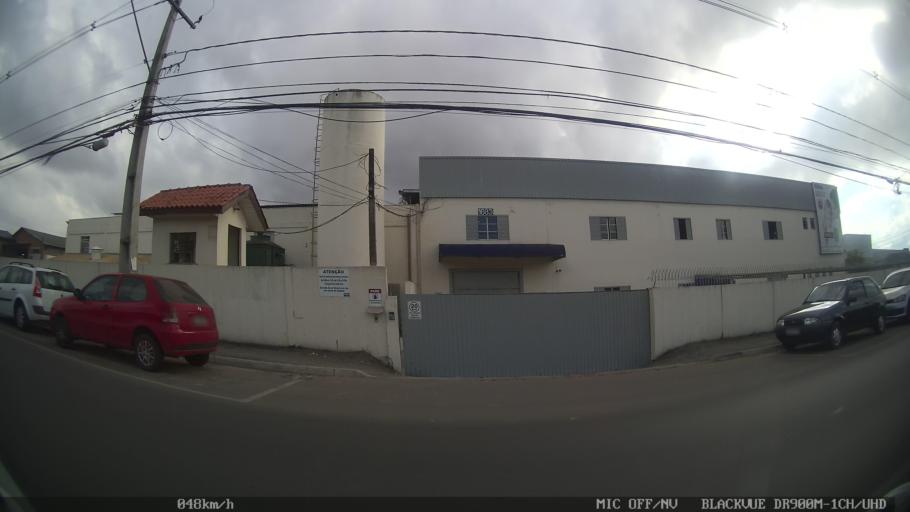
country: BR
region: Parana
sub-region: Pinhais
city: Pinhais
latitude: -25.4141
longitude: -49.1907
